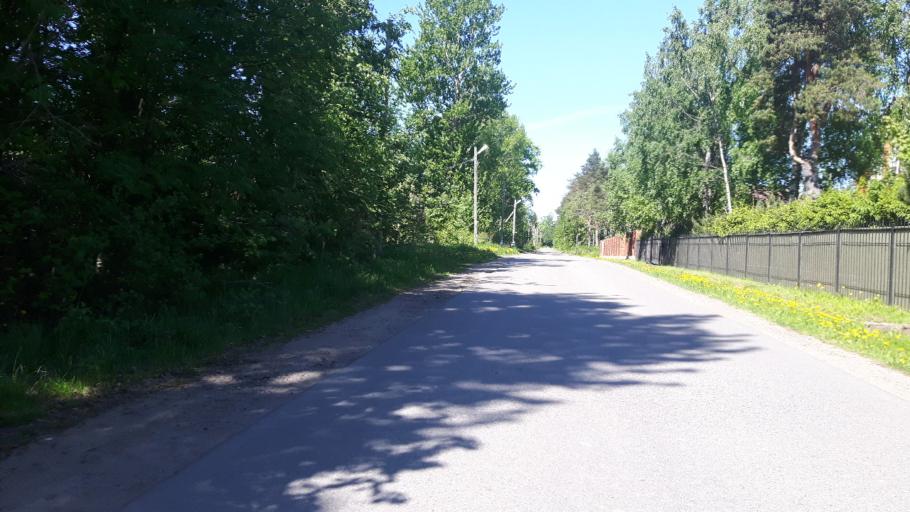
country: RU
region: Leningrad
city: Lebyazh'ye
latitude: 59.9697
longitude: 29.3898
